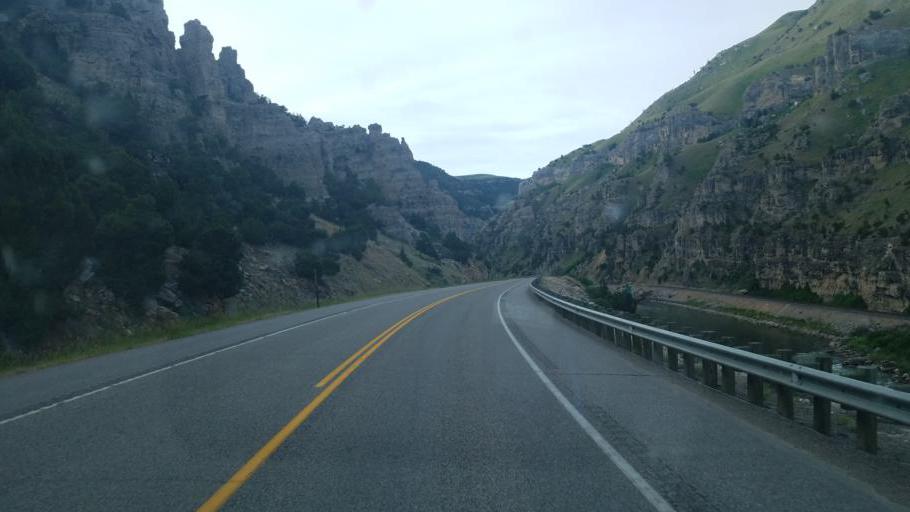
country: US
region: Wyoming
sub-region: Hot Springs County
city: Thermopolis
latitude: 43.5498
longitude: -108.1923
